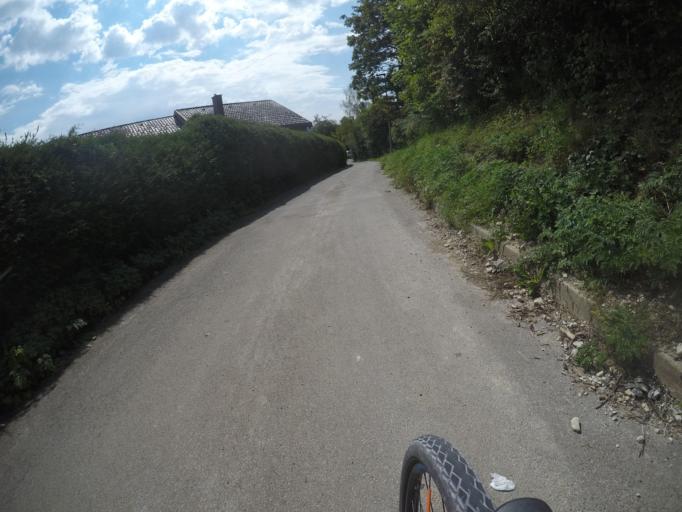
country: DE
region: Baden-Wuerttemberg
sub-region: Tuebingen Region
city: Munsingen
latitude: 48.4165
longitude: 9.4988
